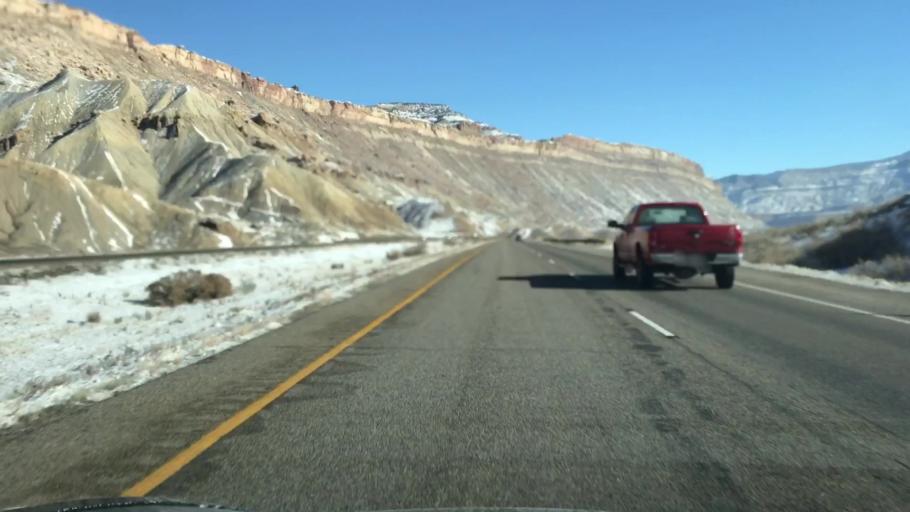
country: US
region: Colorado
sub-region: Mesa County
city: Palisade
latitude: 39.1165
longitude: -108.3937
